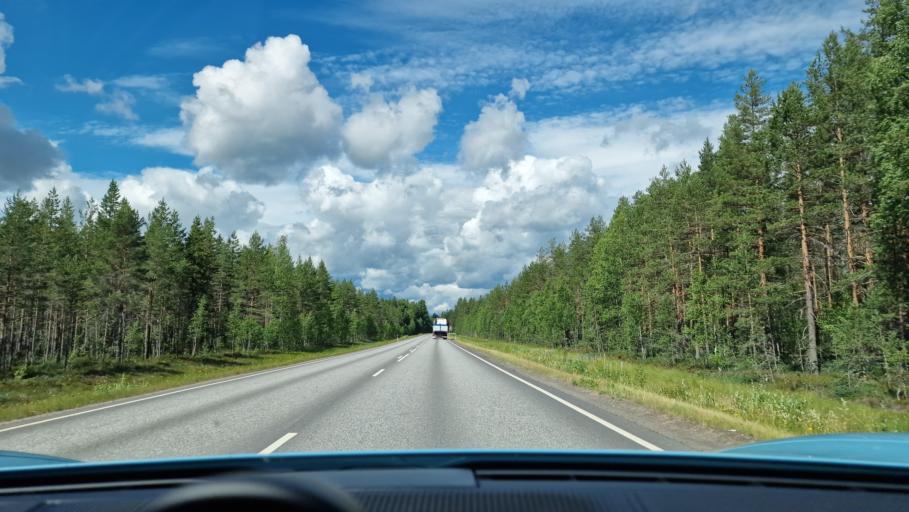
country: FI
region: Pirkanmaa
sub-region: Ylae-Pirkanmaa
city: Juupajoki
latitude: 61.8502
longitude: 24.2181
